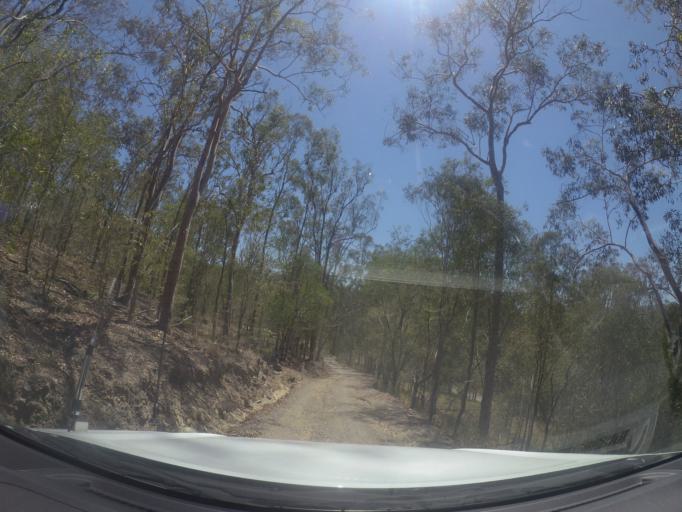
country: AU
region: Queensland
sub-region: Logan
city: Windaroo
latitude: -27.8054
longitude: 153.1686
